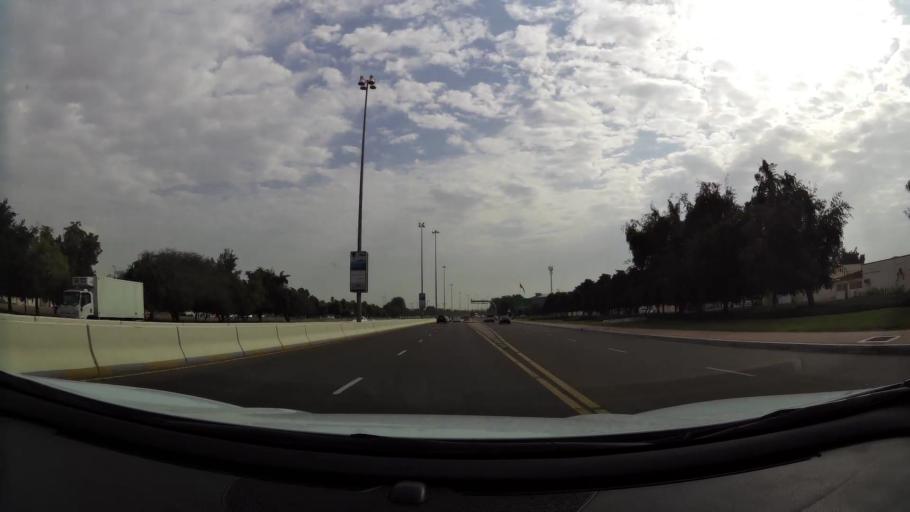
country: AE
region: Abu Dhabi
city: Al Ain
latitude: 24.2221
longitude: 55.7190
